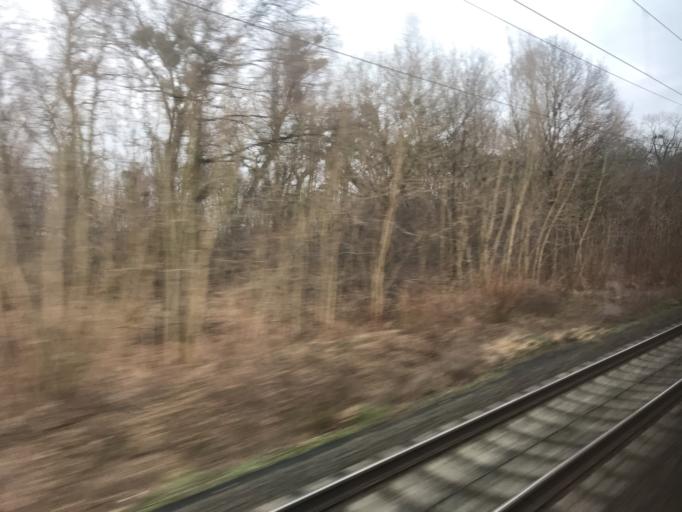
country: DE
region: Lower Saxony
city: Wolfsburg
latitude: 52.4306
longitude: 10.8350
